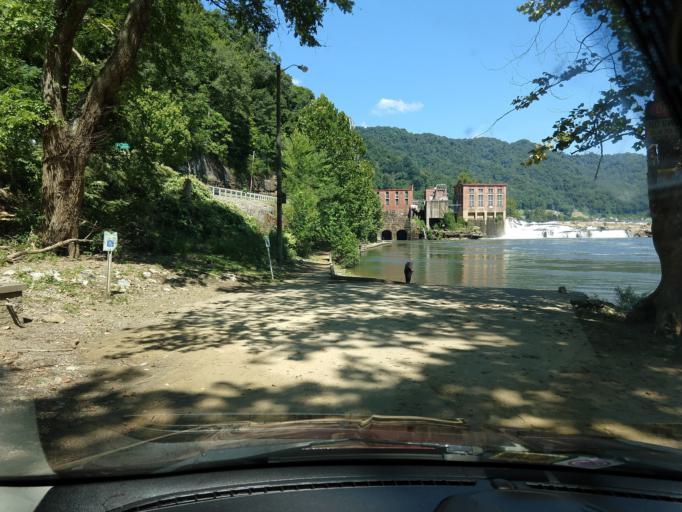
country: US
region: West Virginia
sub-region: Fayette County
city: Ansted
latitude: 38.1465
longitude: -81.2139
